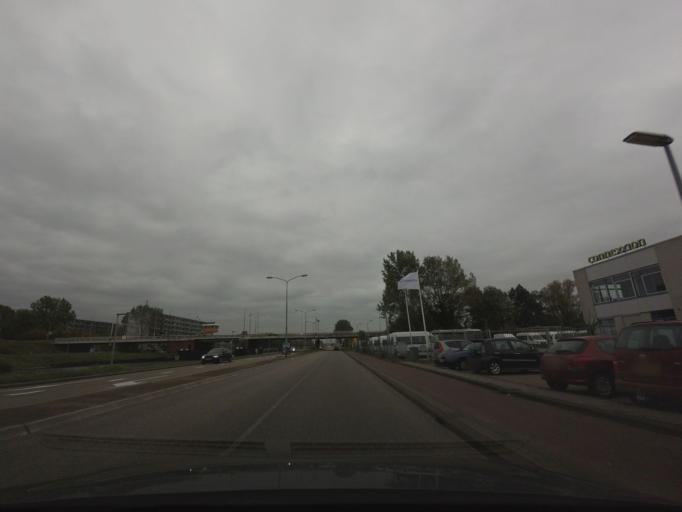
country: NL
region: North Holland
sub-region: Gemeente Alkmaar
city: Alkmaar
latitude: 52.6475
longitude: 4.7430
